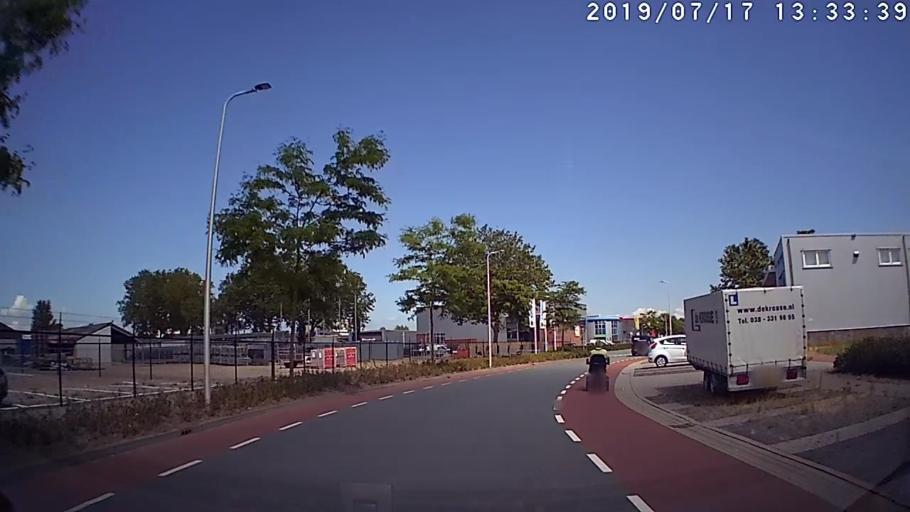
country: NL
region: Overijssel
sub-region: Gemeente Kampen
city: Kampen
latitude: 52.5598
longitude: 5.8877
